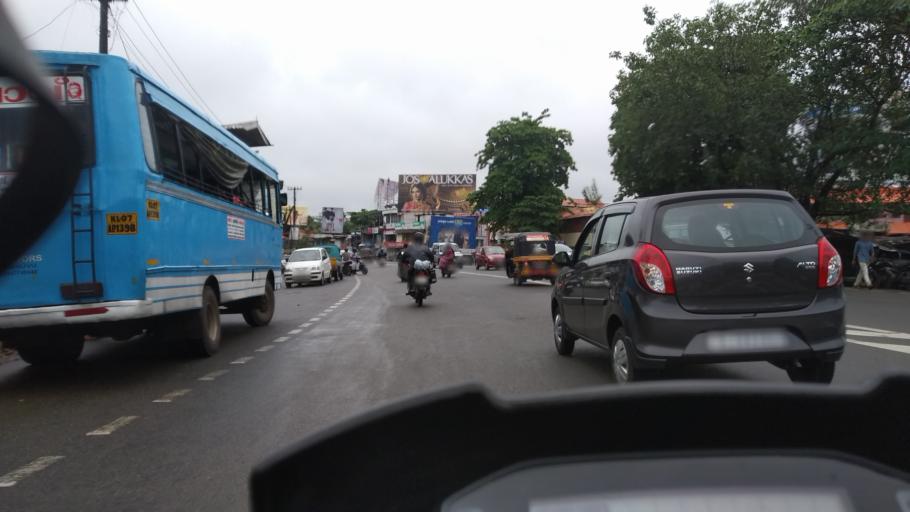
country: IN
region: Kerala
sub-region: Alappuzha
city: Mavelikara
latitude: 9.2800
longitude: 76.4590
